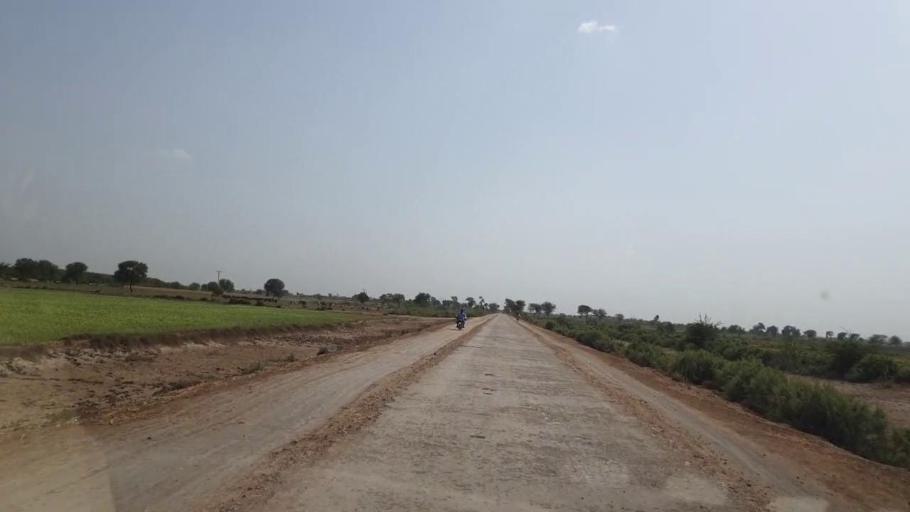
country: PK
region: Sindh
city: Rajo Khanani
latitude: 25.0209
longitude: 68.8730
